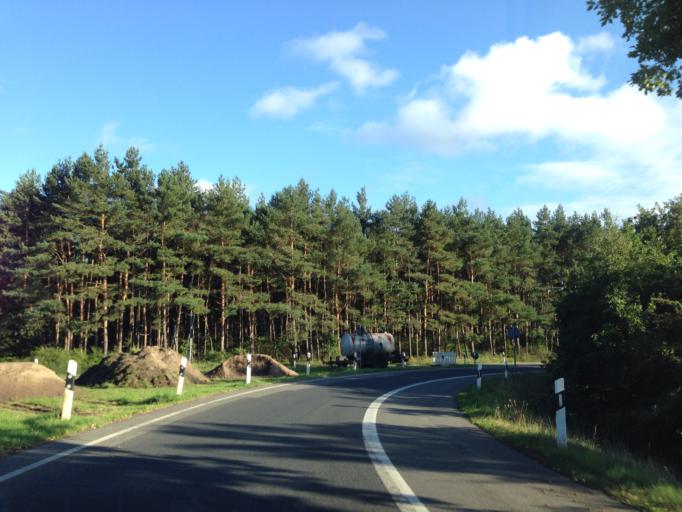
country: DE
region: Lower Saxony
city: Wendisch Evern
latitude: 53.2374
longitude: 10.4766
